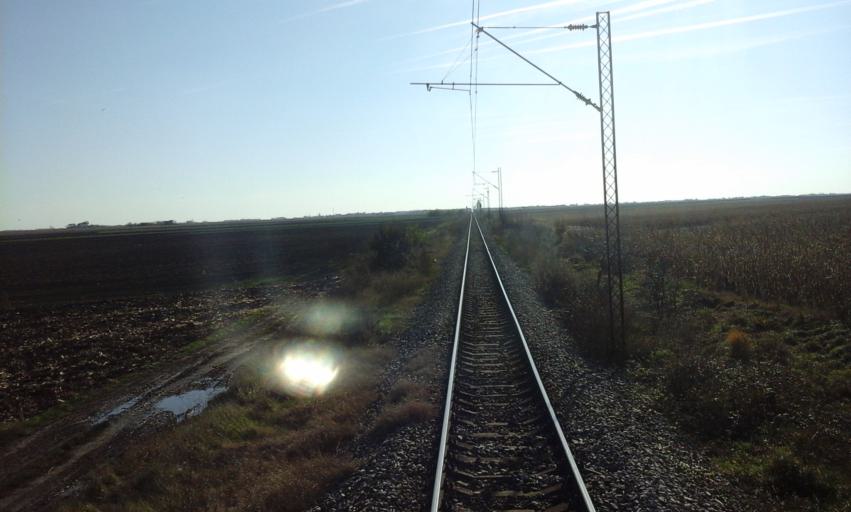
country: RS
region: Autonomna Pokrajina Vojvodina
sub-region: Severnobacki Okrug
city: Subotica
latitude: 45.9766
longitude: 19.6740
